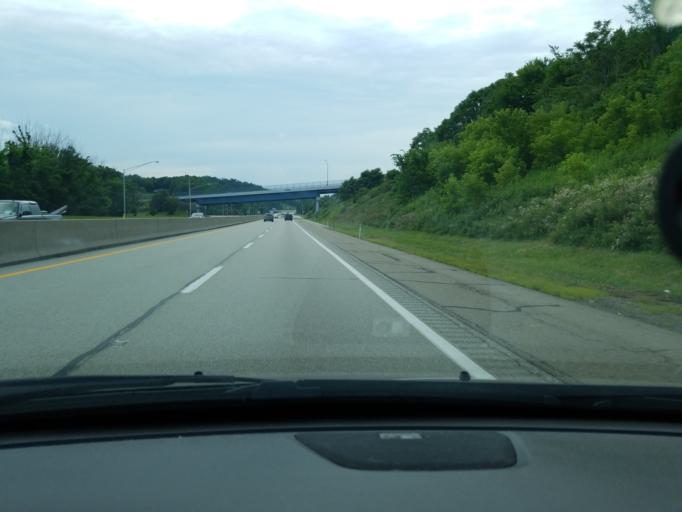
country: US
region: Pennsylvania
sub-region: Beaver County
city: Big Beaver
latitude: 40.8364
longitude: -80.3769
